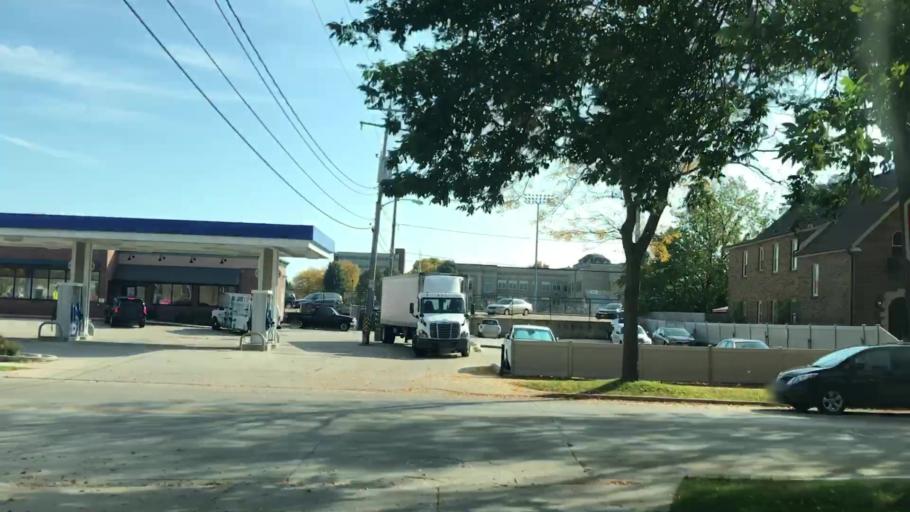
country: US
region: Wisconsin
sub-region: Milwaukee County
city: Shorewood
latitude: 43.0886
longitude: -87.8926
